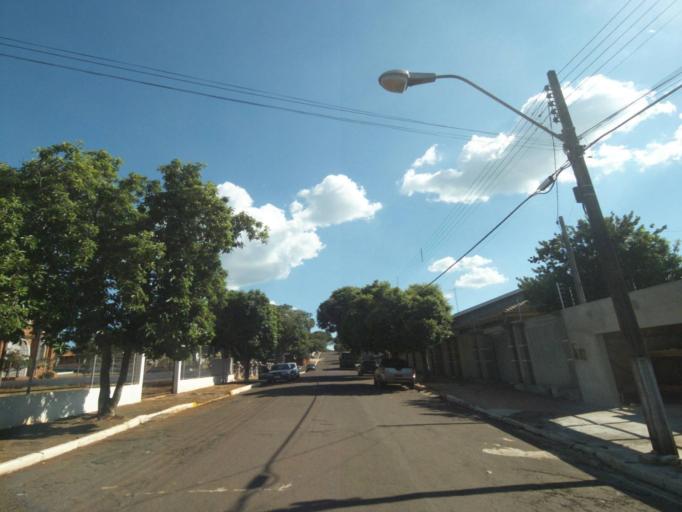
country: BR
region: Parana
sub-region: Sertanopolis
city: Sertanopolis
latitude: -23.0372
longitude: -50.8155
